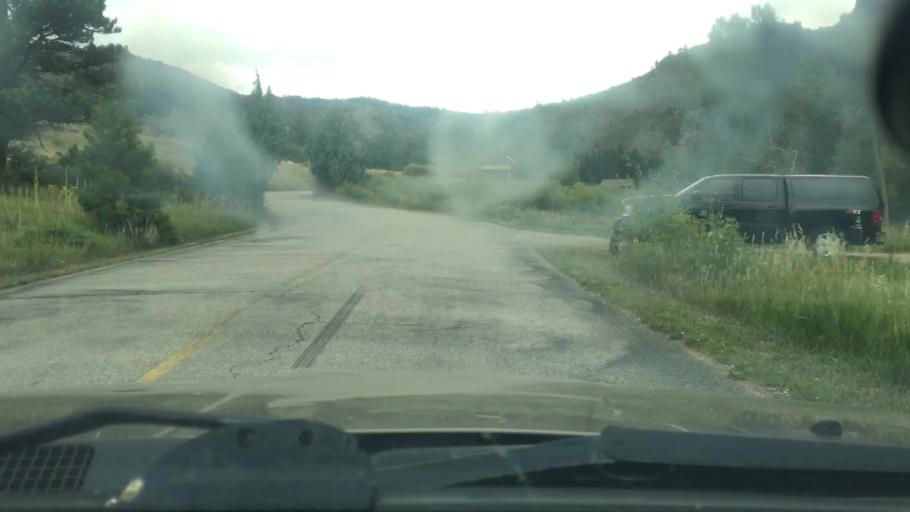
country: US
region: Colorado
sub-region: Larimer County
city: Laporte
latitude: 40.6954
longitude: -105.4460
